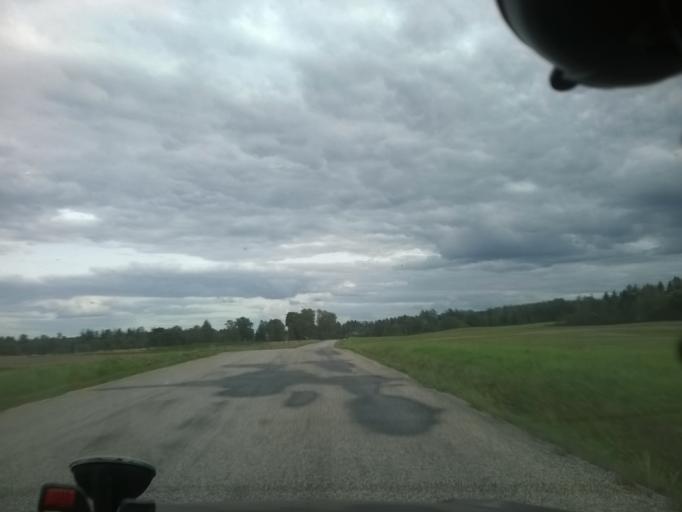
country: EE
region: Vorumaa
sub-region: Voru linn
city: Voru
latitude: 57.8082
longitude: 27.0769
